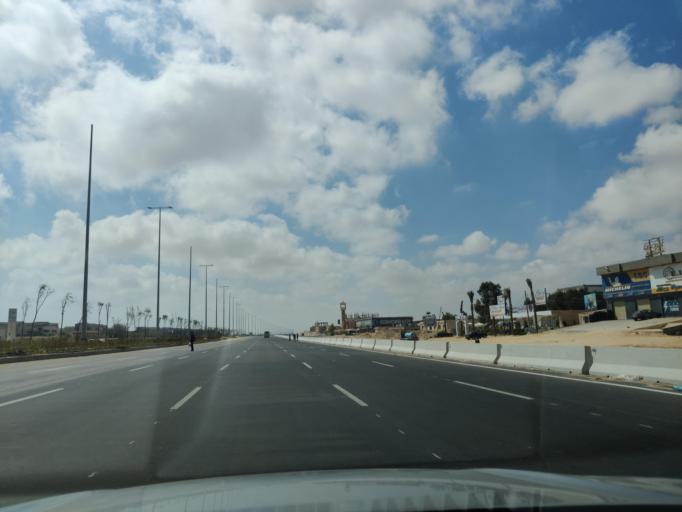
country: EG
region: Muhafazat Matruh
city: Al `Alamayn
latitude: 30.9431
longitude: 28.7800
